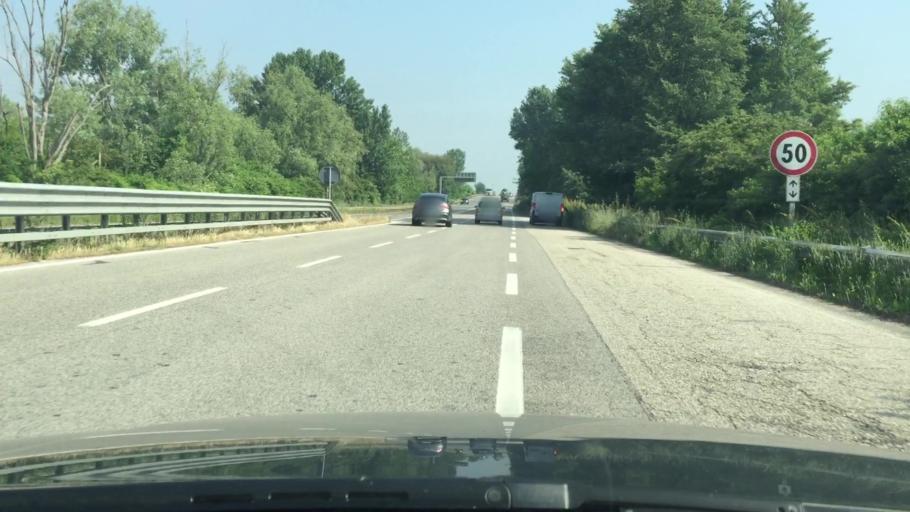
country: IT
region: Emilia-Romagna
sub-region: Provincia di Ferrara
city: Gaibanella-Sant'Edigio
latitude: 44.7976
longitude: 11.6370
